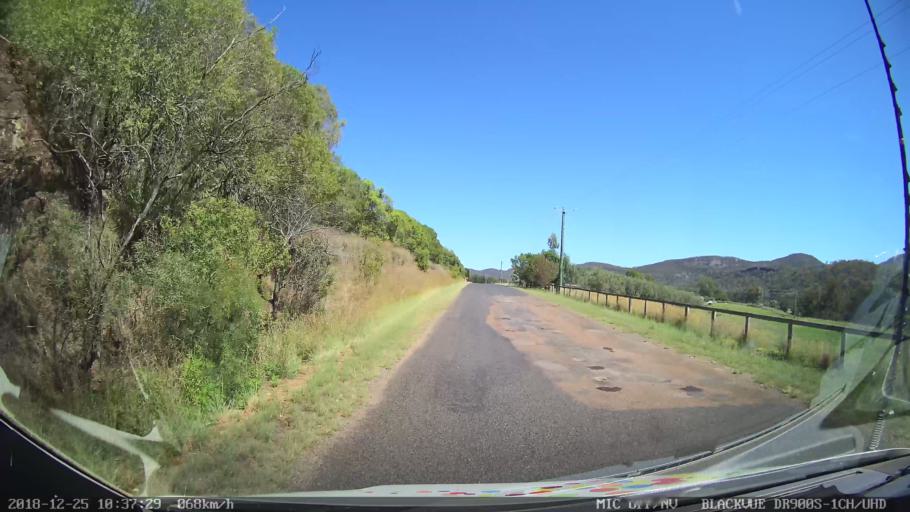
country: AU
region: New South Wales
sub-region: Upper Hunter Shire
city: Merriwa
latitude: -32.4090
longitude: 150.3777
